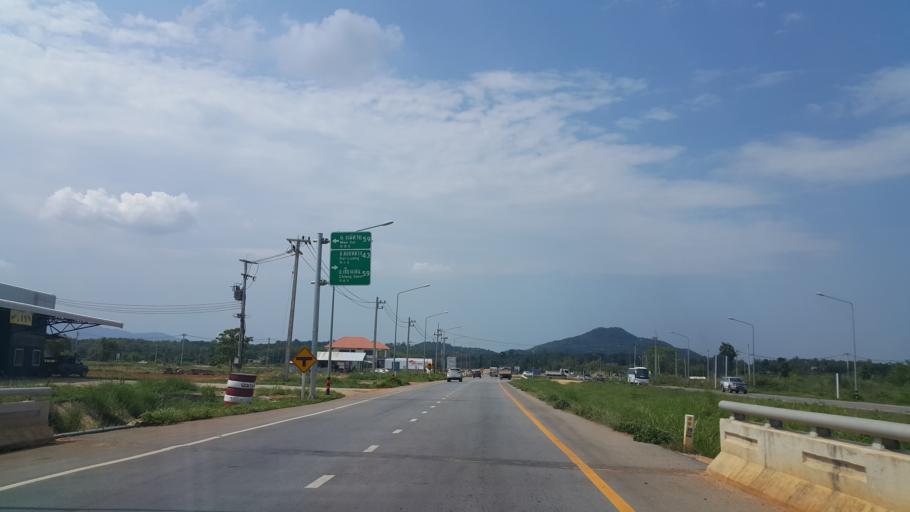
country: TH
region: Chiang Rai
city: Chiang Rai
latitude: 20.0025
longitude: 99.8930
